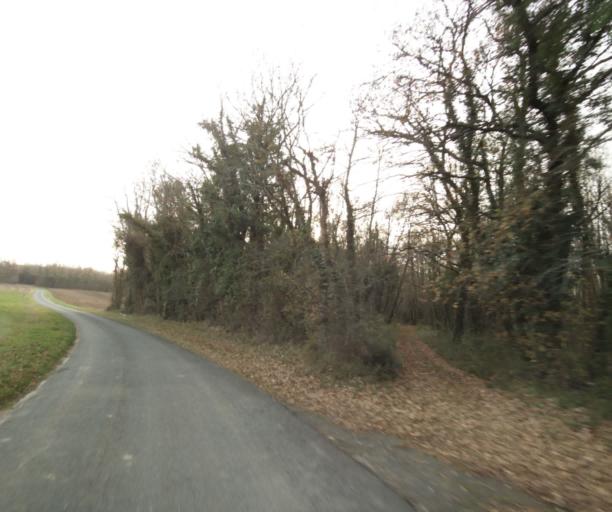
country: FR
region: Poitou-Charentes
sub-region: Departement de la Charente-Maritime
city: Saint-Hilaire-de-Villefranche
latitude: 45.8307
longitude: -0.5706
